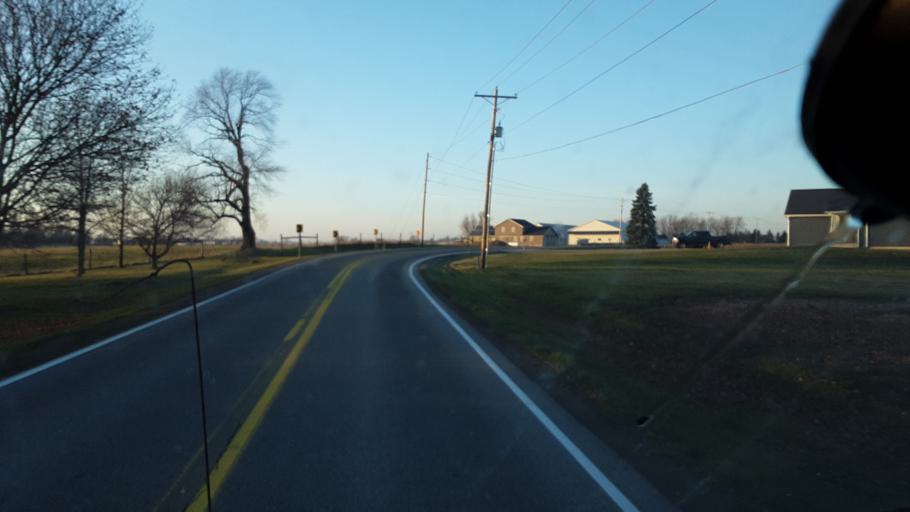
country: US
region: Indiana
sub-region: Allen County
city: Harlan
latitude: 41.1873
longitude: -84.9404
